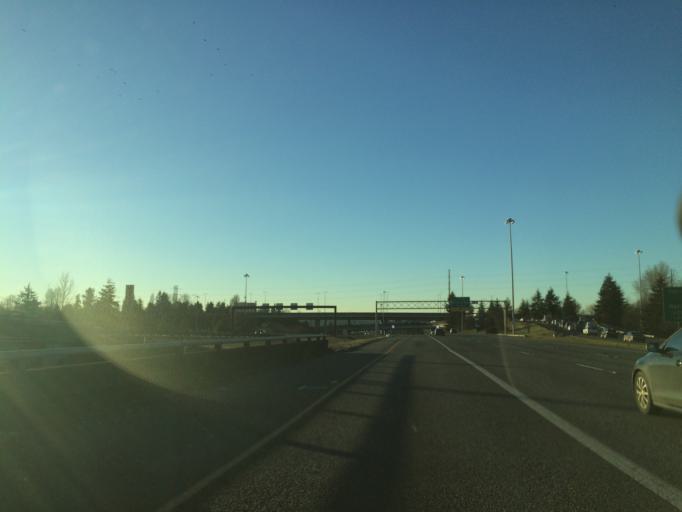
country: US
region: Washington
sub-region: King County
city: Newport
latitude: 47.5804
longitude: -122.1684
